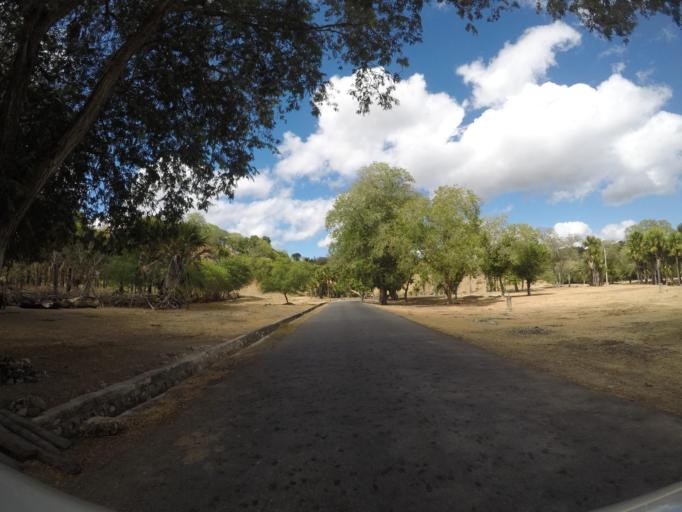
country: TL
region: Lautem
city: Lospalos
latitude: -8.4076
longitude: 126.8284
